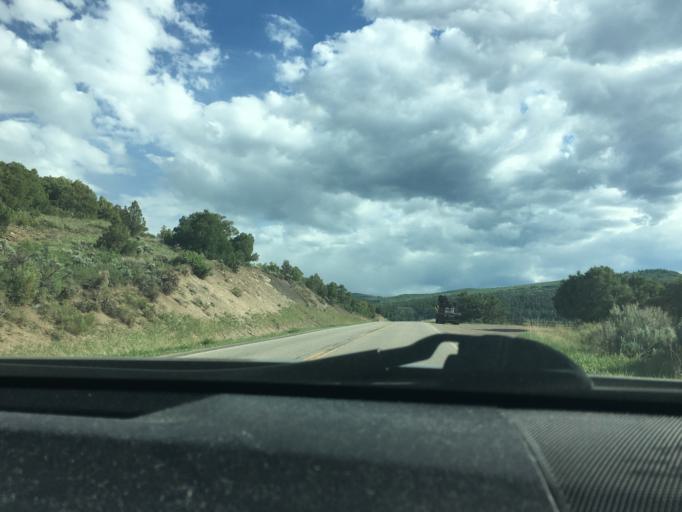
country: US
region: Colorado
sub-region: Eagle County
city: Edwards
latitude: 39.7112
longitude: -106.6849
